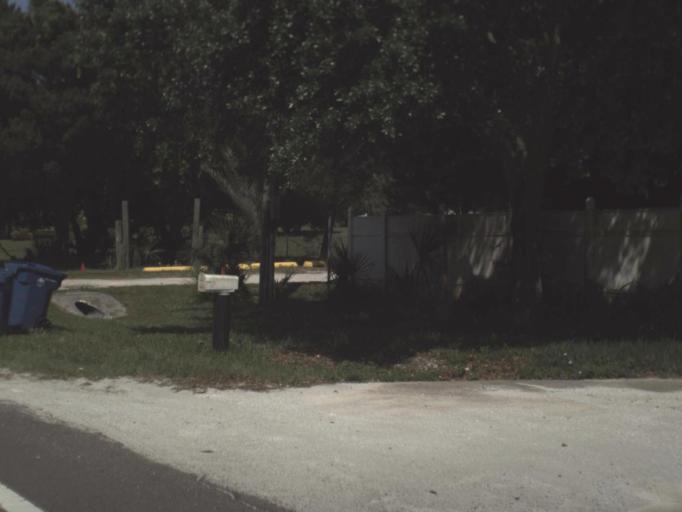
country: US
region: Florida
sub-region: Duval County
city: Atlantic Beach
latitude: 30.4036
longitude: -81.4313
